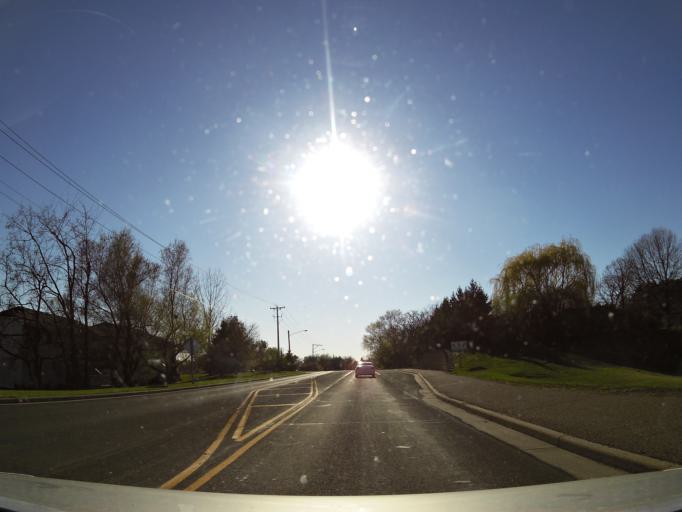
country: US
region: Wisconsin
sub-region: Saint Croix County
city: Hudson
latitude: 44.9778
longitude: -92.7324
